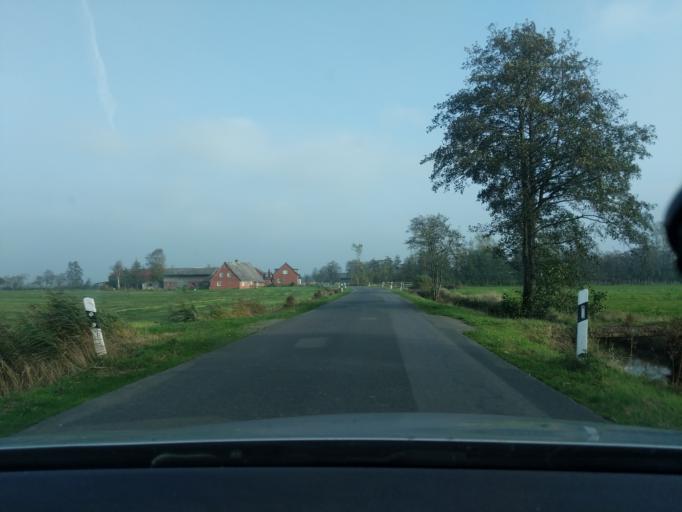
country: DE
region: Lower Saxony
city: Wanna
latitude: 53.7258
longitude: 8.8292
